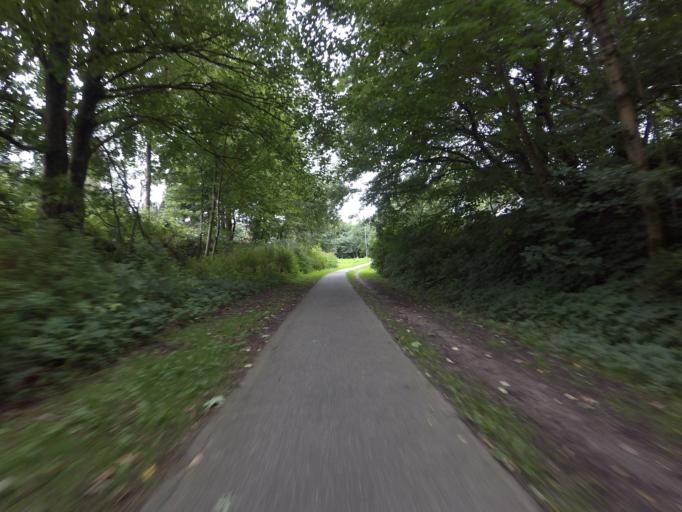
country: DK
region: Central Jutland
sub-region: Silkeborg Kommune
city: Virklund
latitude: 56.0979
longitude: 9.5503
